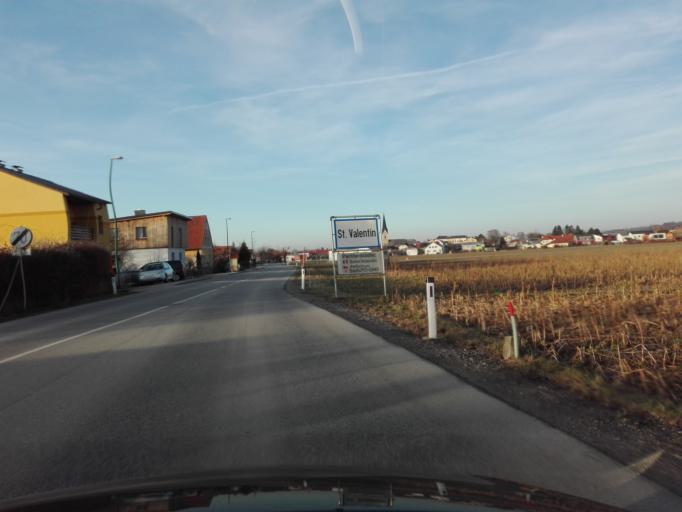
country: AT
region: Lower Austria
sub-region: Politischer Bezirk Amstetten
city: Sankt Valentin
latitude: 48.1681
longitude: 14.5309
